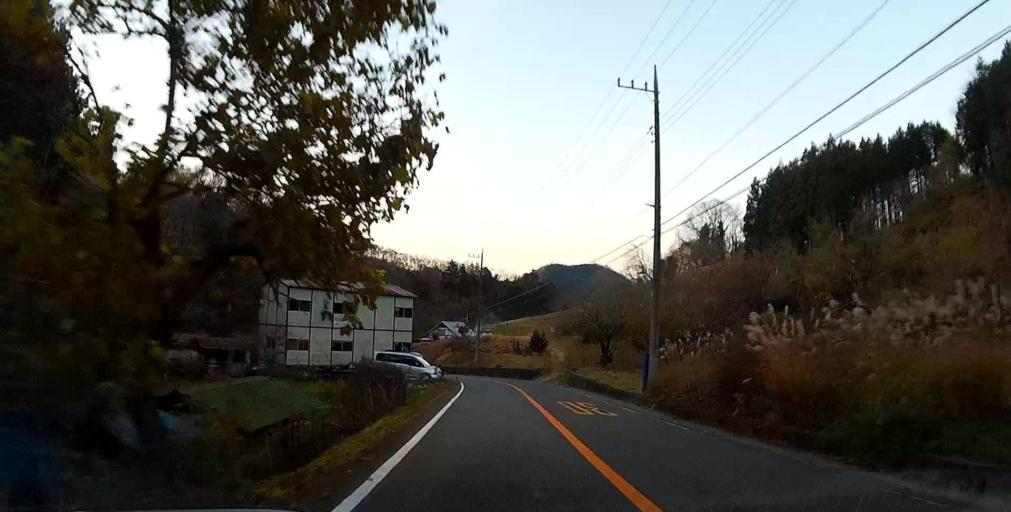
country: JP
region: Yamanashi
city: Uenohara
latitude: 35.5851
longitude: 139.1742
